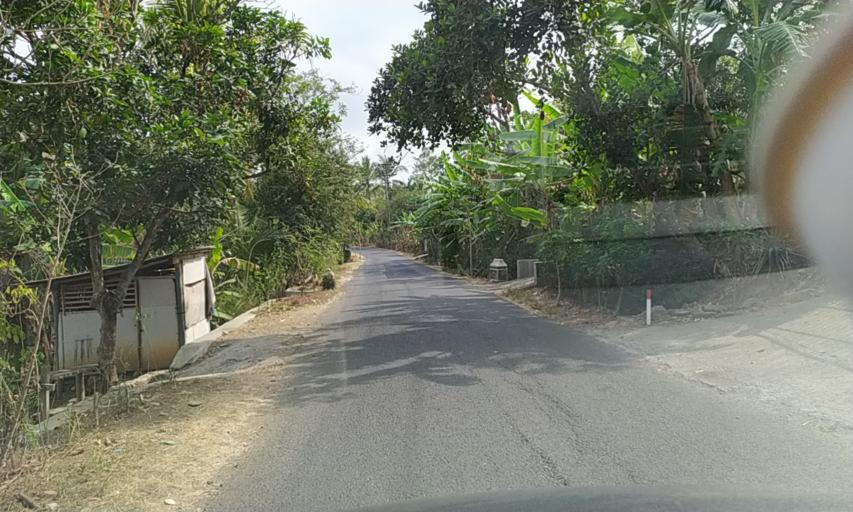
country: ID
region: Central Java
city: Cisuru
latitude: -7.4117
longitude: 108.7364
